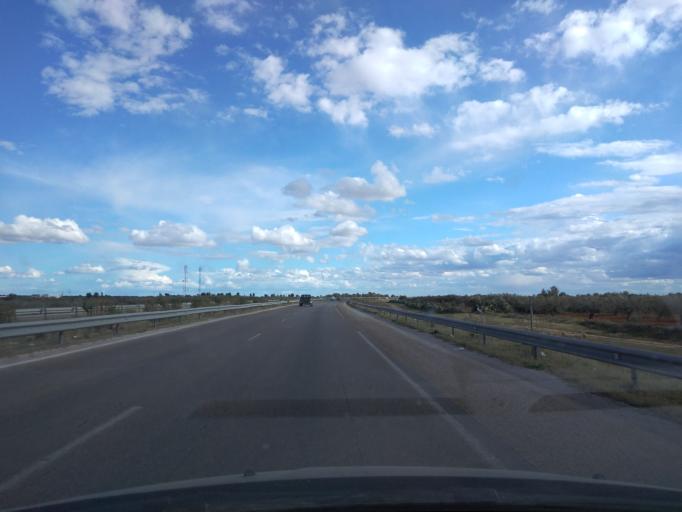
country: TN
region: Al Munastir
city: Manzil Kamil
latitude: 35.6310
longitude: 10.5883
